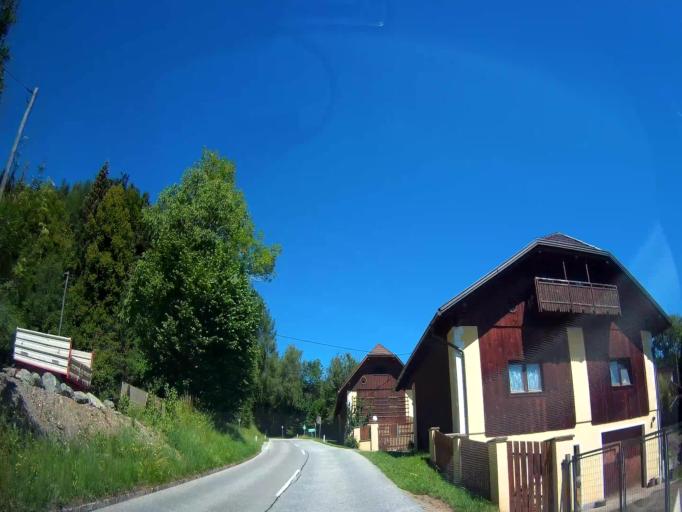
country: AT
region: Carinthia
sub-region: Politischer Bezirk Klagenfurt Land
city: Maria Worth
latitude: 46.6015
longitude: 14.1499
